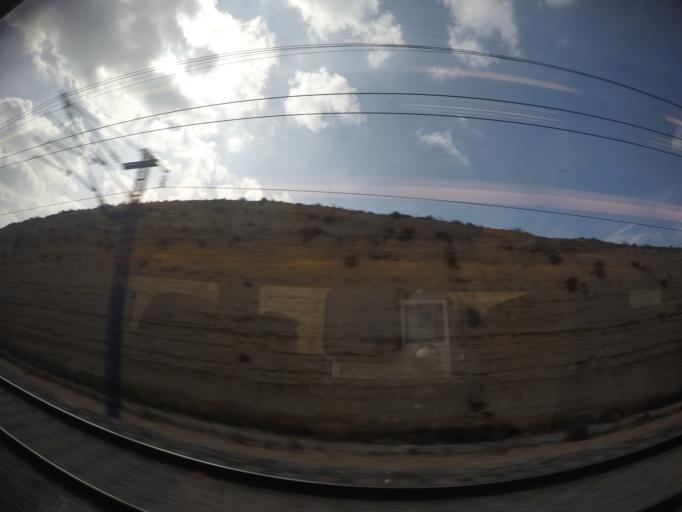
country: ES
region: Aragon
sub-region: Provincia de Zaragoza
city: El Burgo de Ebro
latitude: 41.5570
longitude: -0.7647
